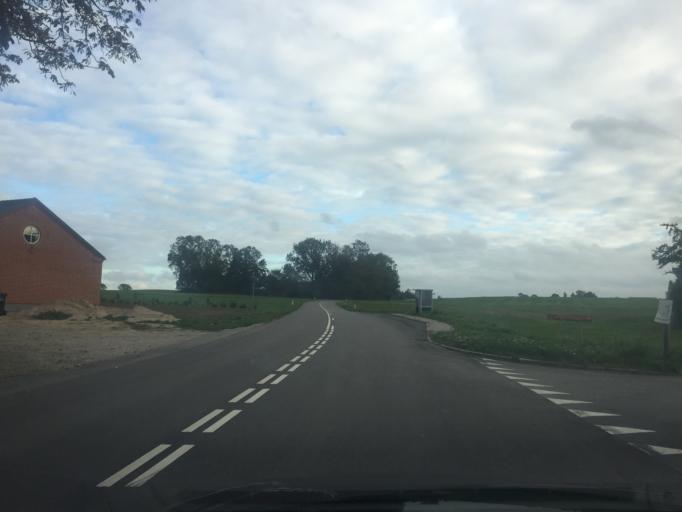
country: DK
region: Zealand
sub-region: Solrod Kommune
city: Havdrup
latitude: 55.5674
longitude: 12.1128
